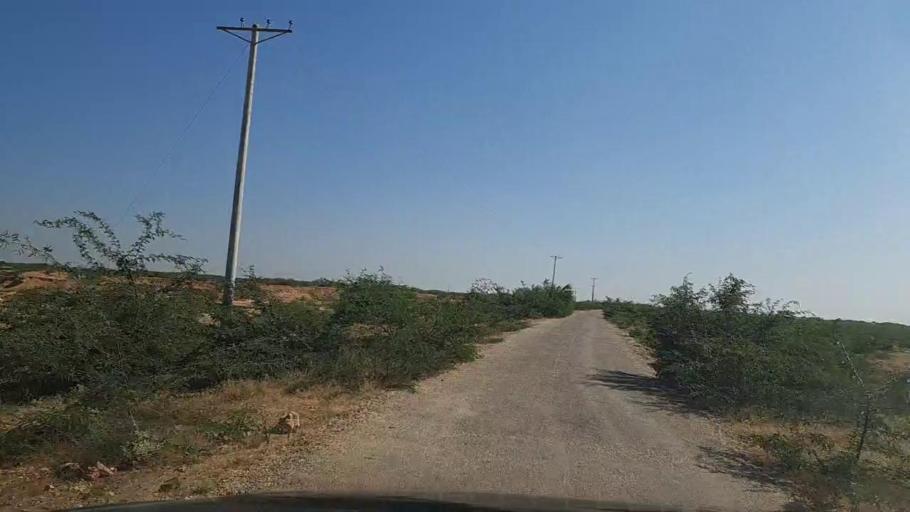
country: PK
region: Sindh
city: Thatta
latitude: 24.6299
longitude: 67.8363
